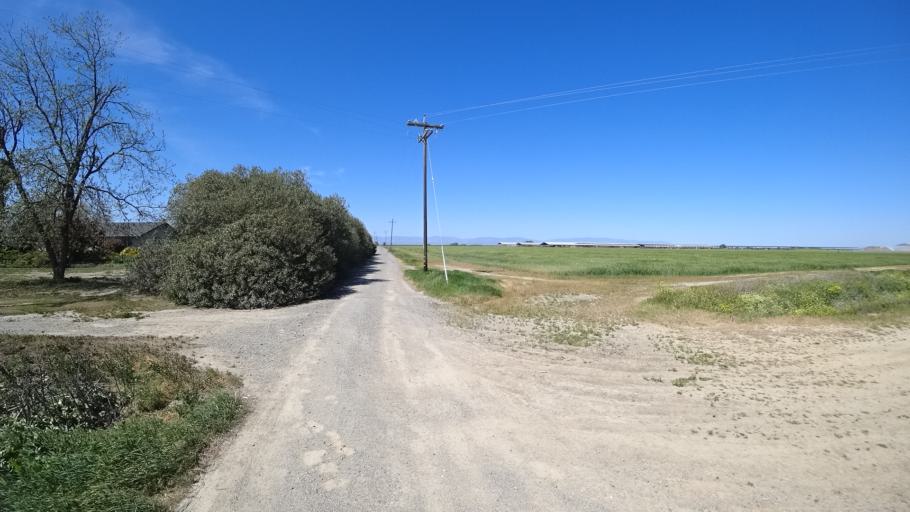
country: US
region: California
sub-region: Glenn County
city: Orland
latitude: 39.6382
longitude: -122.1226
